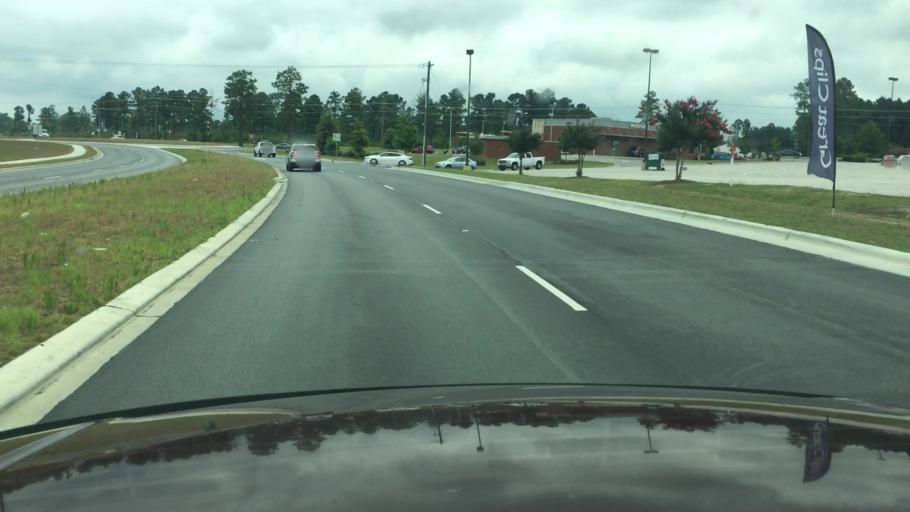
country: US
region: North Carolina
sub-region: Cumberland County
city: Spring Lake
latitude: 35.2547
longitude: -78.9672
